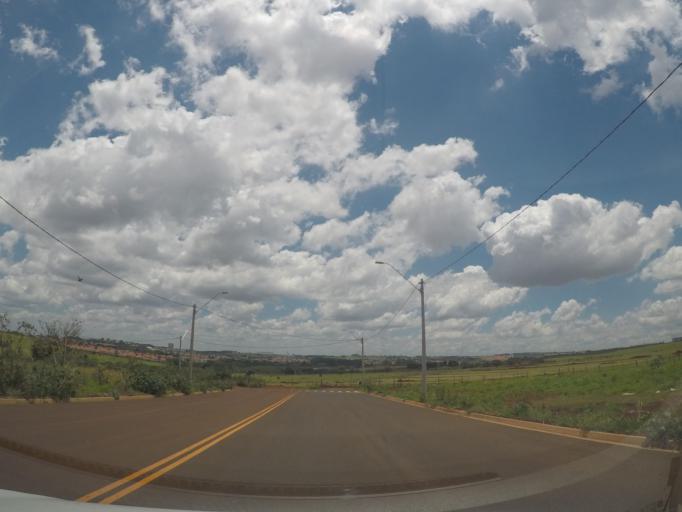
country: BR
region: Sao Paulo
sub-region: Hortolandia
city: Hortolandia
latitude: -22.8364
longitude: -47.2316
